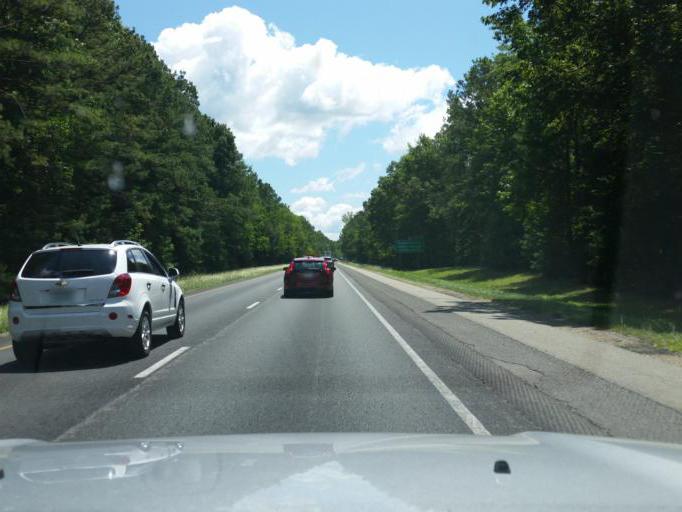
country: US
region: Virginia
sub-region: New Kent County
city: New Kent
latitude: 37.4829
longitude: -76.9389
